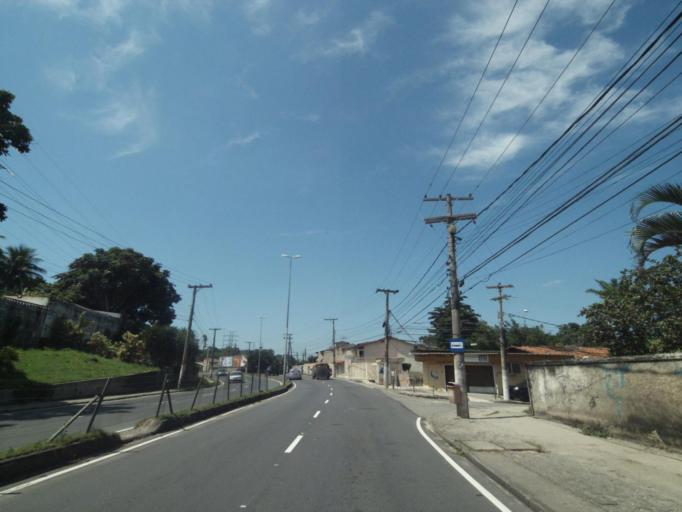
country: BR
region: Rio de Janeiro
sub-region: Sao Goncalo
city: Sao Goncalo
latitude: -22.8816
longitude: -43.0286
